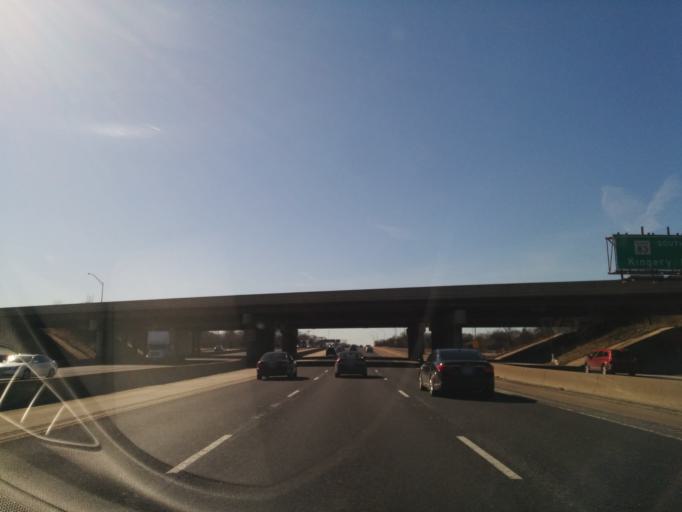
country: US
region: Illinois
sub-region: DuPage County
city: Burr Ridge
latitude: 41.7421
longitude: -87.9434
